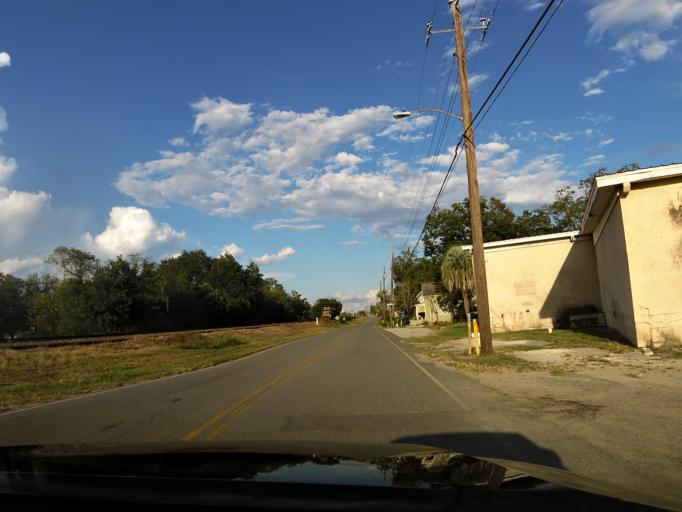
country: US
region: Georgia
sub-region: Lowndes County
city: Valdosta
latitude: 30.8241
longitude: -83.2930
